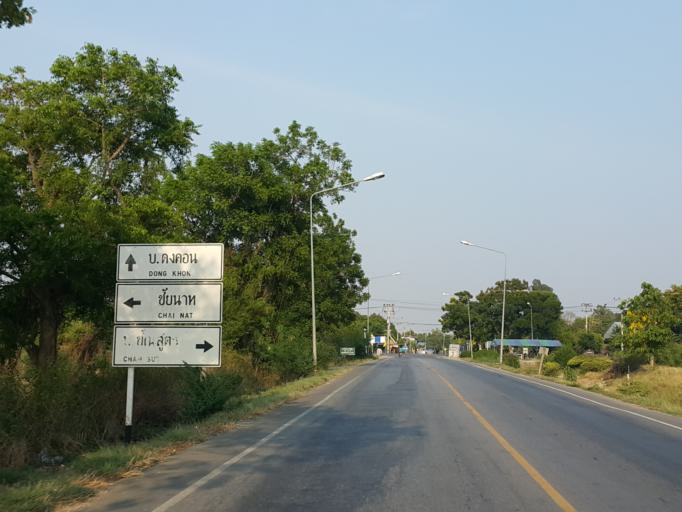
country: TH
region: Chai Nat
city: Sankhaburi
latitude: 15.0214
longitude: 100.1431
